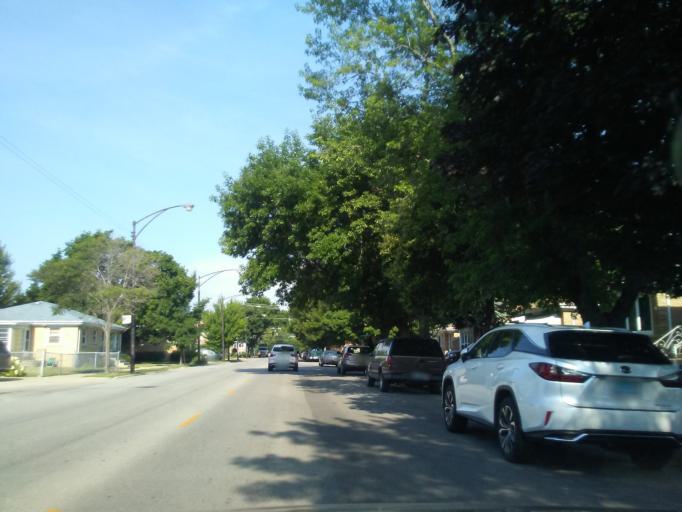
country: US
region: Illinois
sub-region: Cook County
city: Lincolnwood
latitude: 41.9830
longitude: -87.7663
